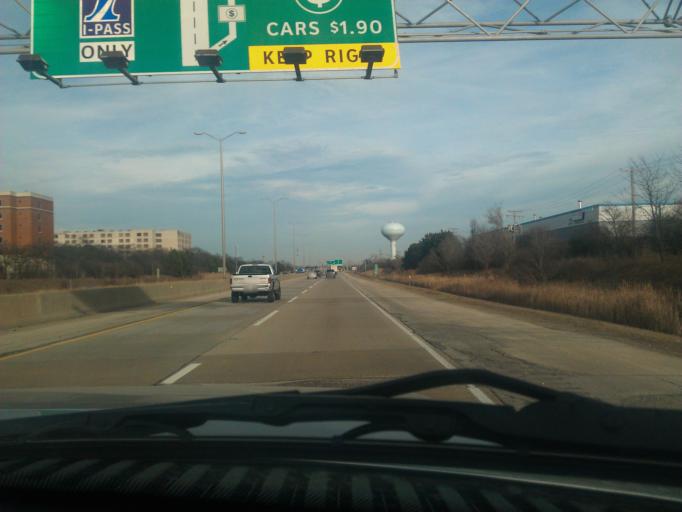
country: US
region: Illinois
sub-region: Lake County
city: Riverwoods
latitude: 42.1495
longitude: -87.8699
